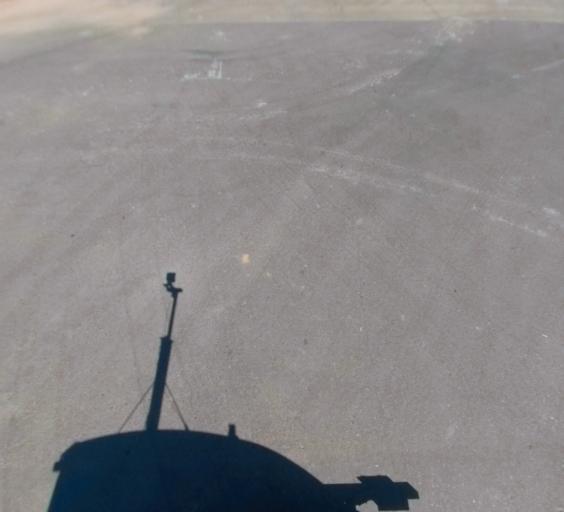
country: US
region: California
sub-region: Madera County
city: Bonadelle Ranchos-Madera Ranchos
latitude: 36.9184
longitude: -119.8035
